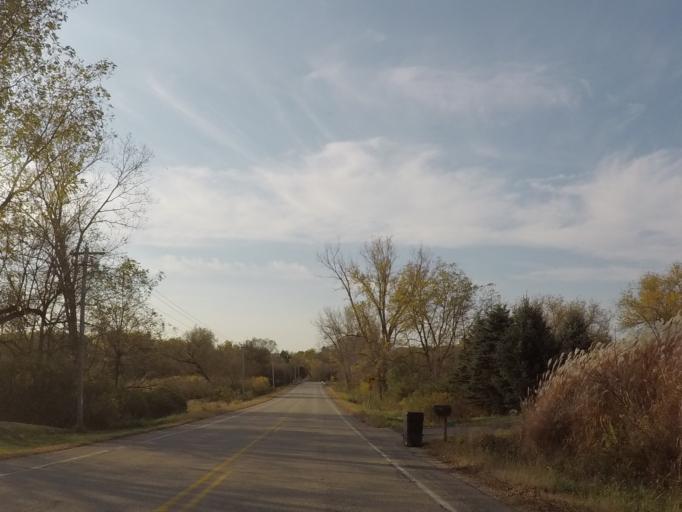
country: US
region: Wisconsin
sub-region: Dane County
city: Cross Plains
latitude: 43.0274
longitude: -89.6216
